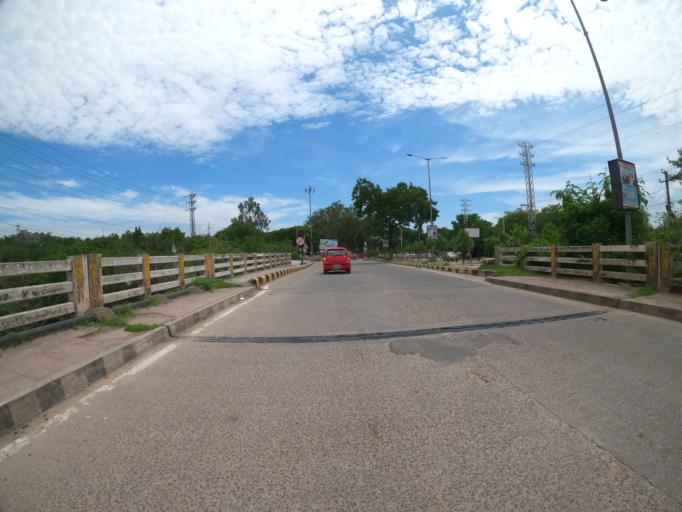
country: IN
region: Telangana
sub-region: Hyderabad
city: Hyderabad
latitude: 17.3725
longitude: 78.4052
